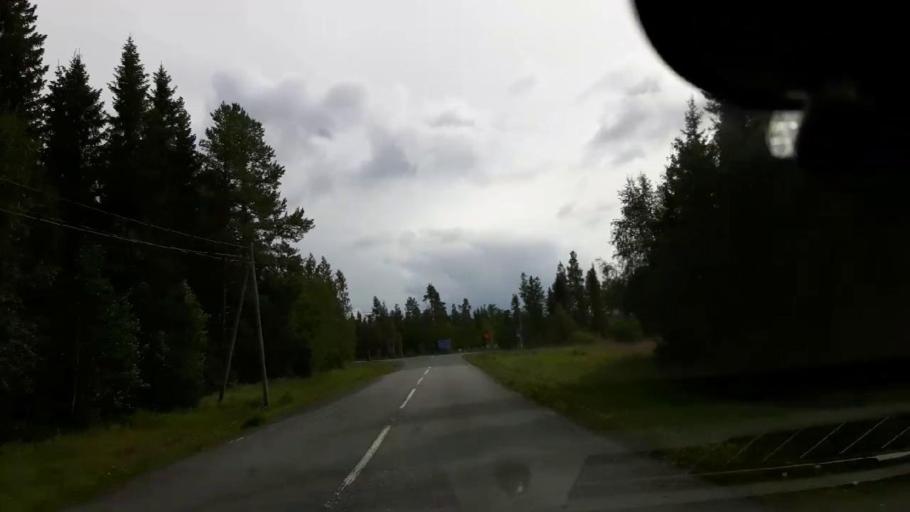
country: SE
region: Jaemtland
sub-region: Krokoms Kommun
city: Valla
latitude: 63.3876
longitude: 13.8199
